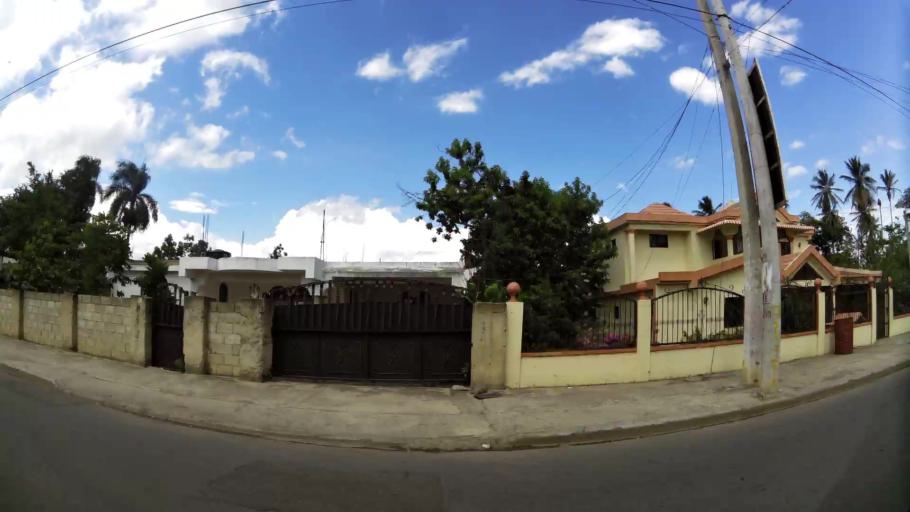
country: DO
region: Santiago
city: Licey al Medio
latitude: 19.3883
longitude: -70.6346
